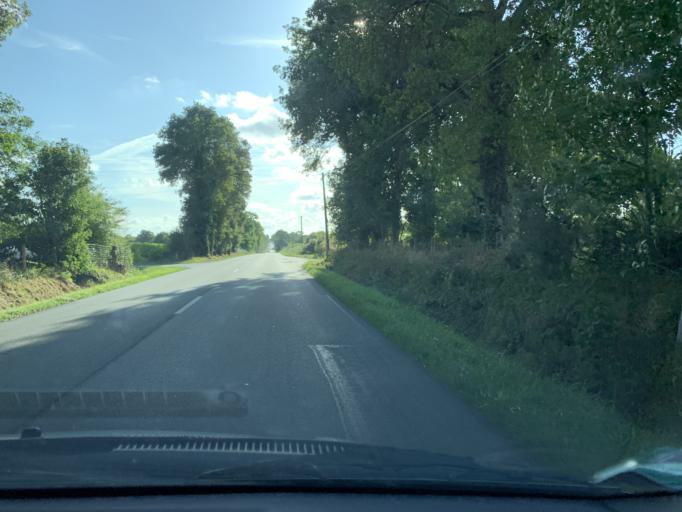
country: FR
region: Brittany
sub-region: Departement du Morbihan
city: Ambon
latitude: 47.5567
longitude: -2.5217
